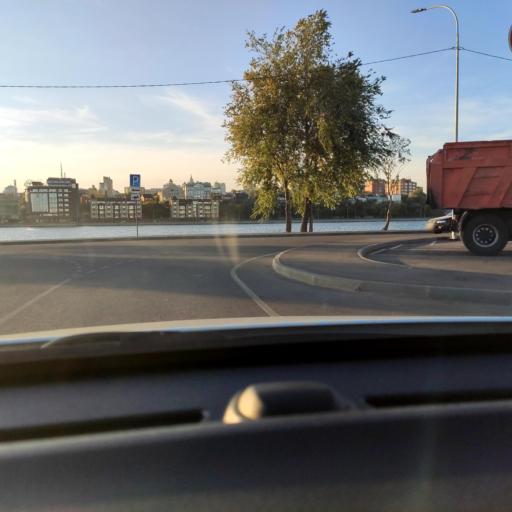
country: RU
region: Voronezj
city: Voronezh
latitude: 51.6682
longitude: 39.2280
